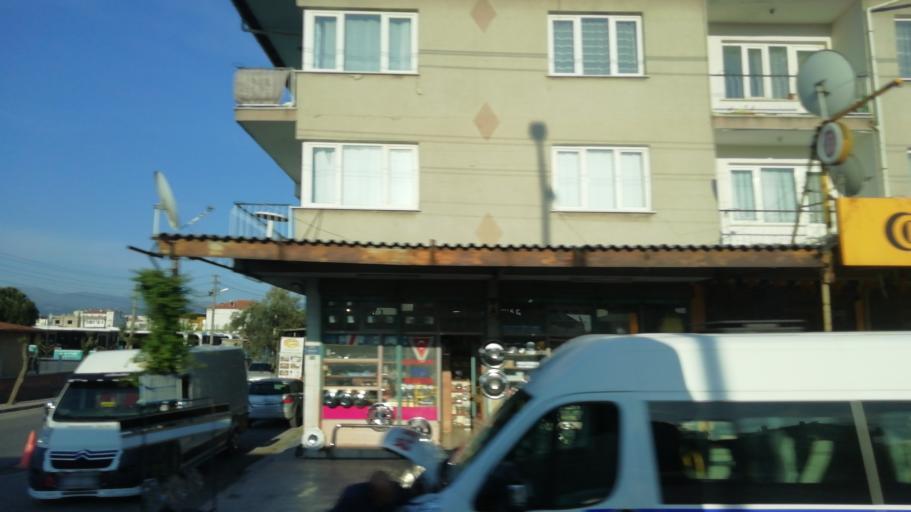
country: TR
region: Manisa
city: Akhisar
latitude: 38.9332
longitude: 27.8349
